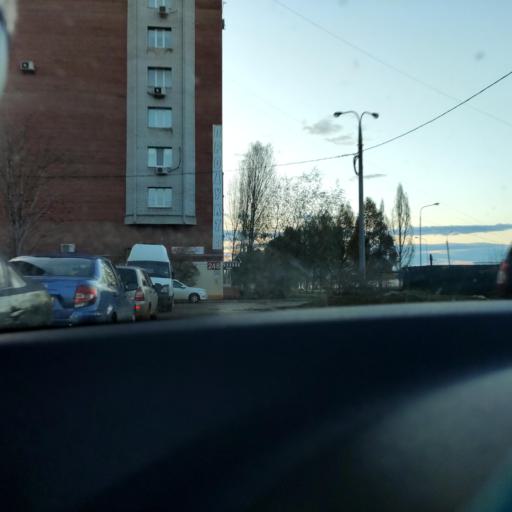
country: RU
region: Samara
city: Samara
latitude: 53.2692
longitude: 50.2198
